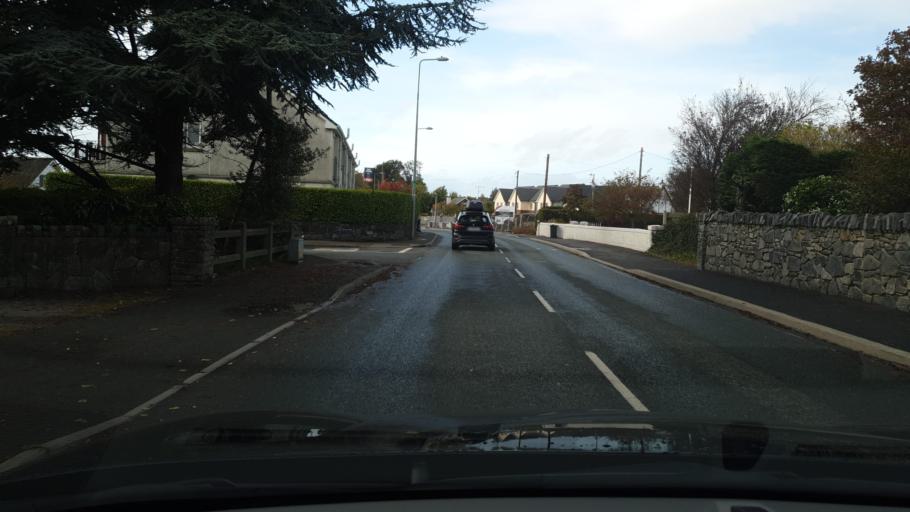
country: IE
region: Leinster
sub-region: An Mhi
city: Ratoath
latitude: 53.5076
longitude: -6.4661
